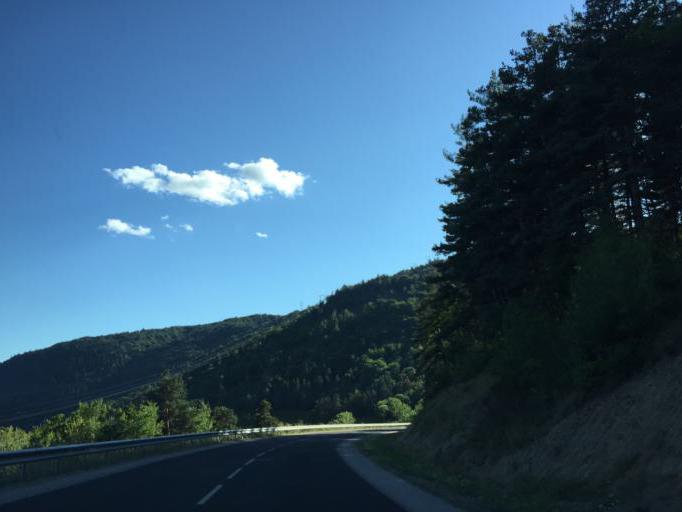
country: FR
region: Auvergne
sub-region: Departement de la Haute-Loire
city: Saugues
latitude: 44.9718
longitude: 3.6295
